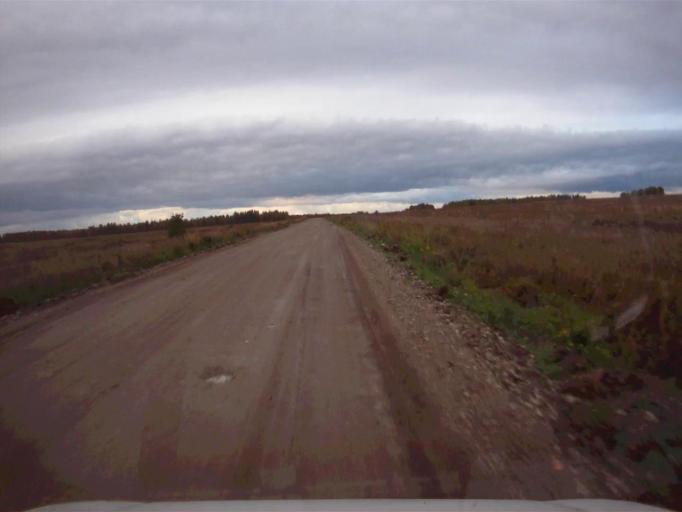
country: RU
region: Sverdlovsk
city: Mikhaylovsk
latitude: 56.1841
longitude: 59.1853
